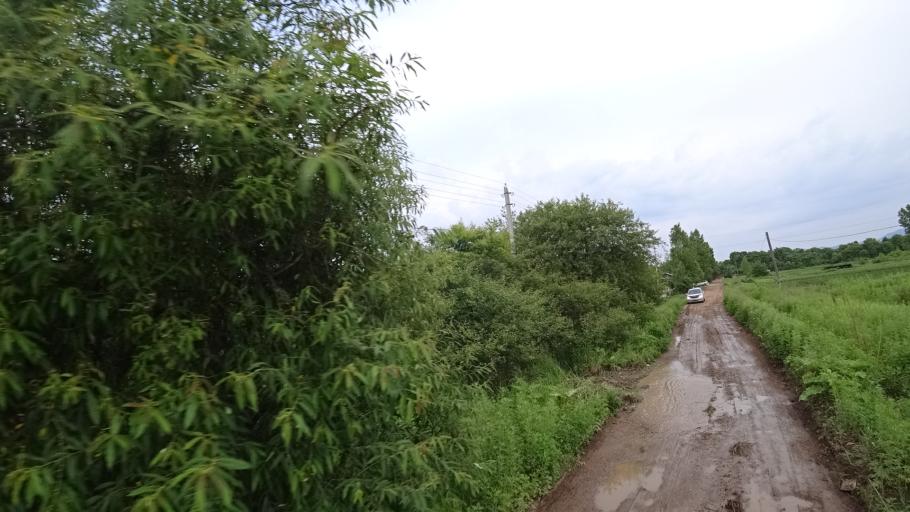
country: RU
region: Primorskiy
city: Novosysoyevka
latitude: 44.2365
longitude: 133.3796
